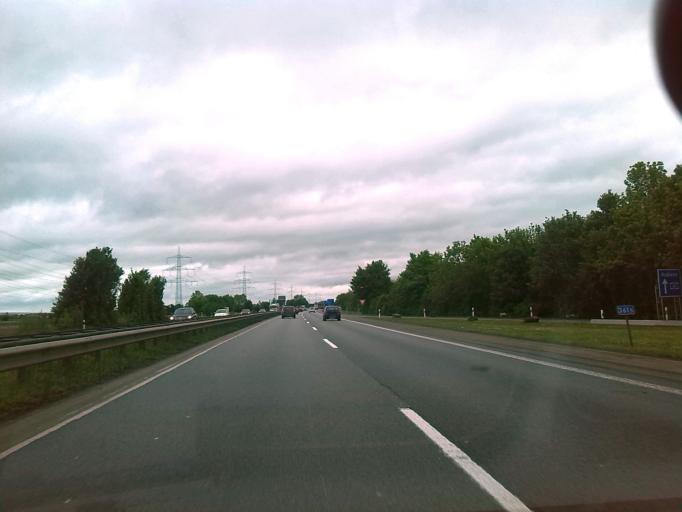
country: DE
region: Rheinland-Pfalz
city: Dannstadt-Schauernheim
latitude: 49.4598
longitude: 8.3149
